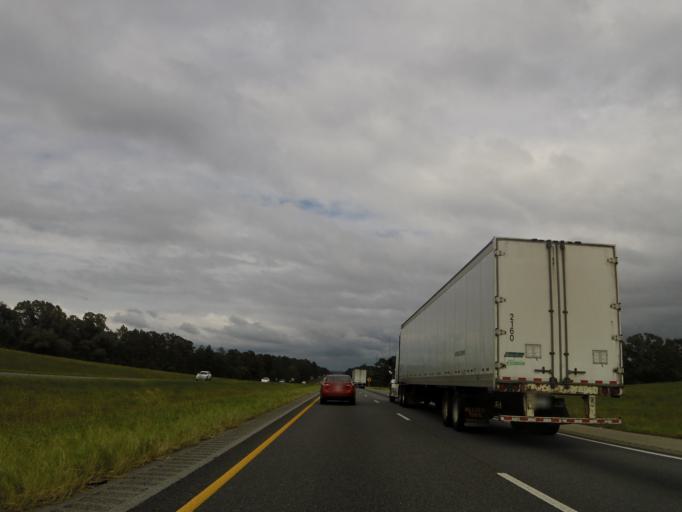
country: US
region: Alabama
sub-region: Escambia County
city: Brewton
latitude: 31.2765
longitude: -87.2047
